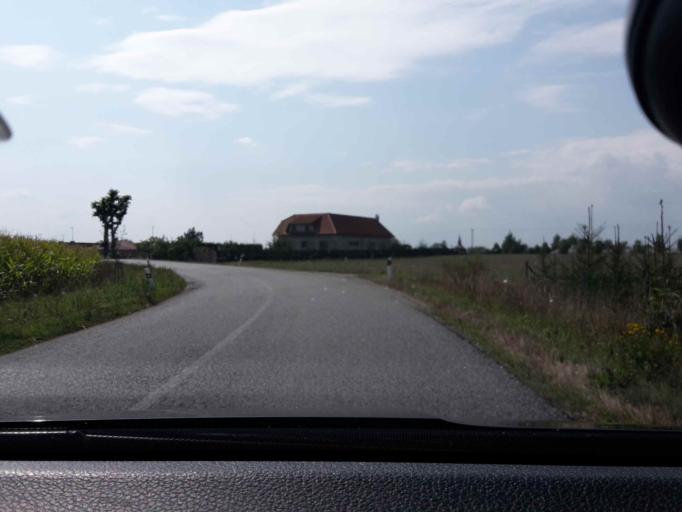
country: CZ
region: Vysocina
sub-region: Okres Jihlava
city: Trest'
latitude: 49.2465
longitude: 15.5613
